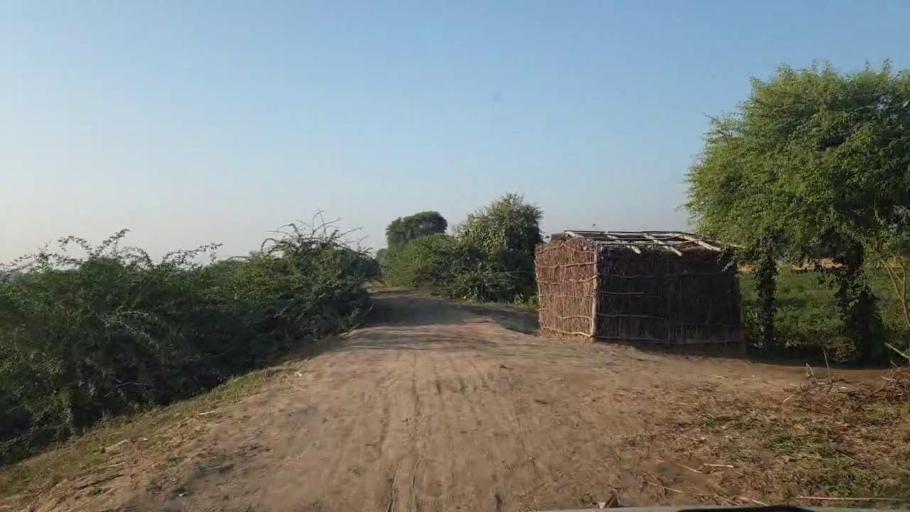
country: PK
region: Sindh
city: Badin
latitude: 24.6118
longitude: 68.7843
